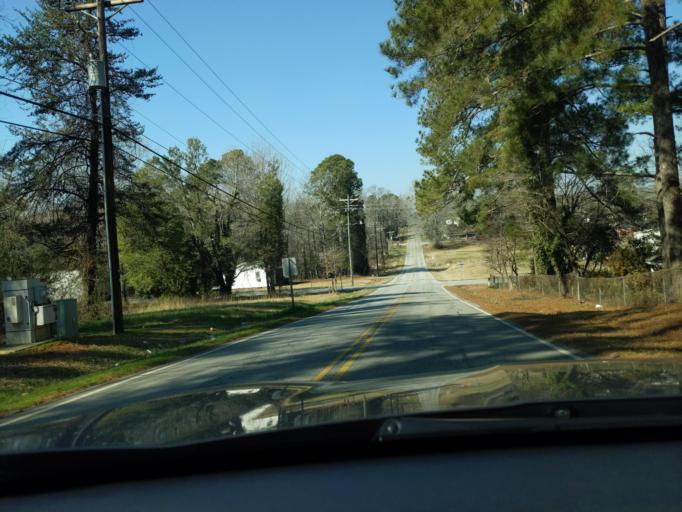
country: US
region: South Carolina
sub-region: Abbeville County
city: Calhoun Falls
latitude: 34.0894
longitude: -82.5920
